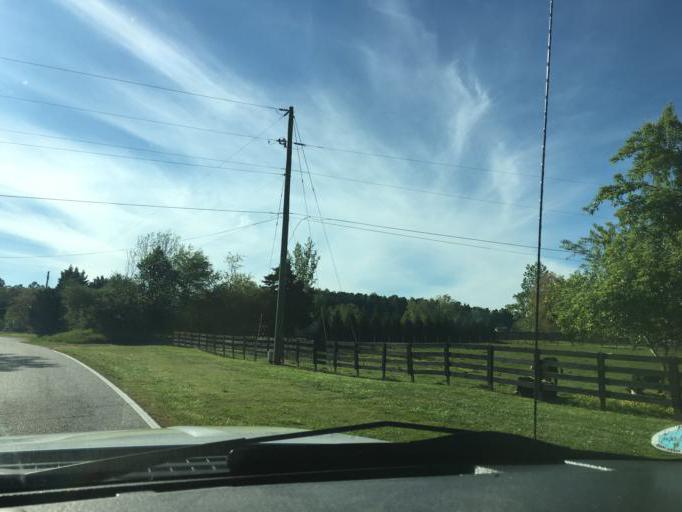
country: US
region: Georgia
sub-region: Dawson County
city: Dawsonville
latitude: 34.3325
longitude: -84.0964
